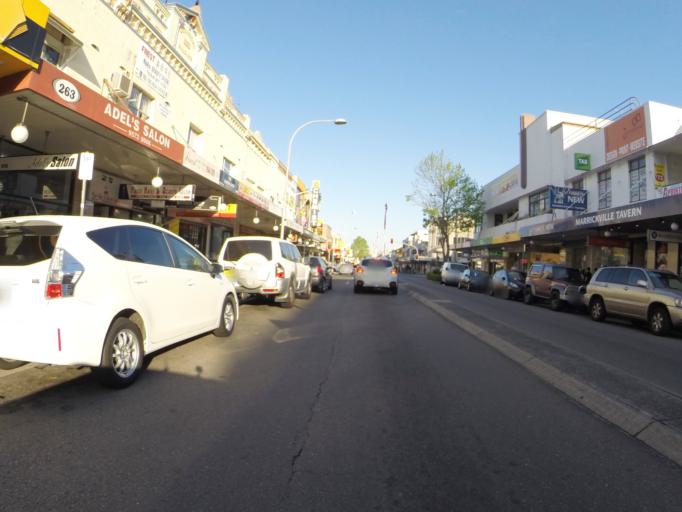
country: AU
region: New South Wales
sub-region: Marrickville
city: Marrickville
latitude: -33.9102
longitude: 151.1557
